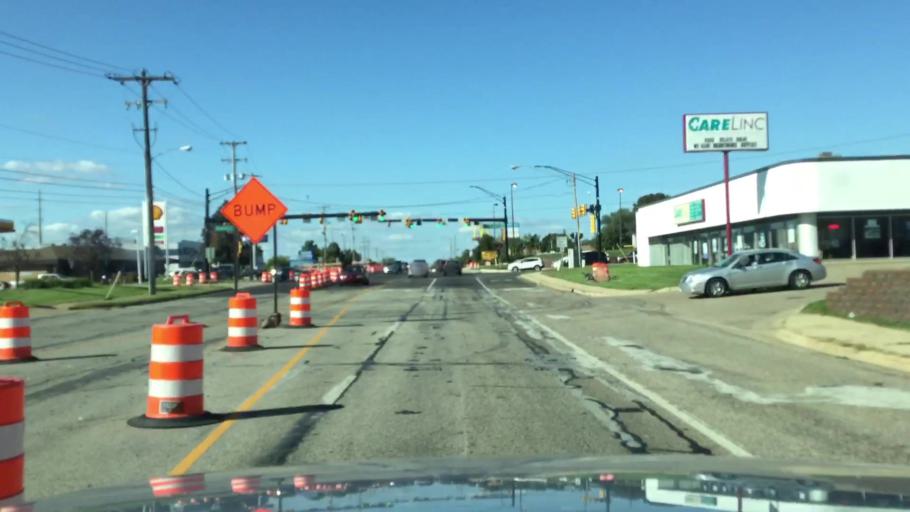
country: US
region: Michigan
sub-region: Kalamazoo County
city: Portage
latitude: 42.2146
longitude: -85.5893
